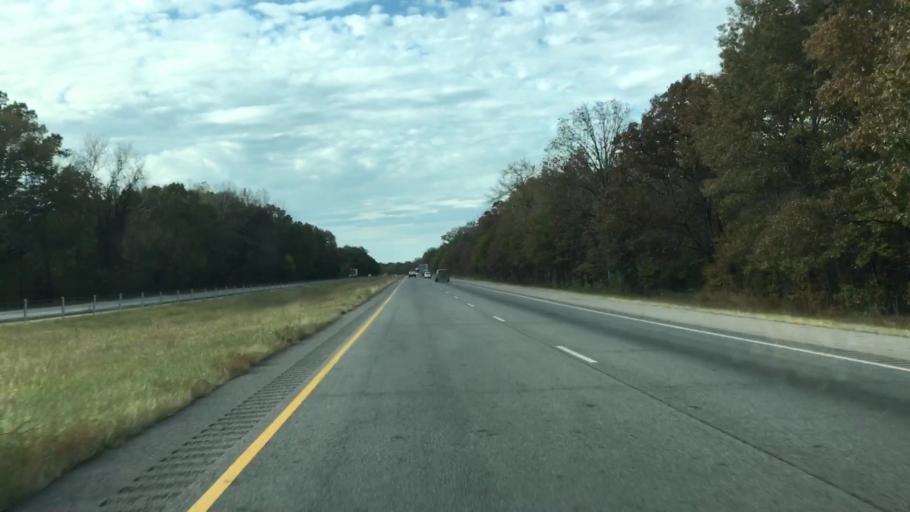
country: US
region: Arkansas
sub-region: Pope County
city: Atkins
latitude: 35.2379
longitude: -92.8548
